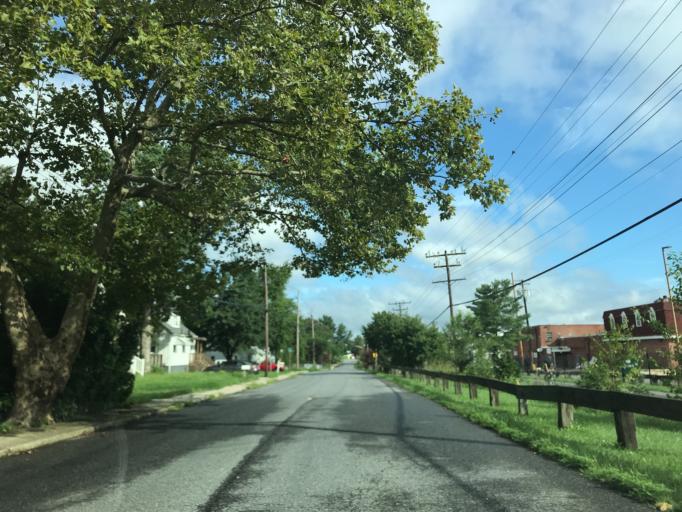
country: US
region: Maryland
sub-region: Anne Arundel County
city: Glen Burnie
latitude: 39.1590
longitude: -76.6215
